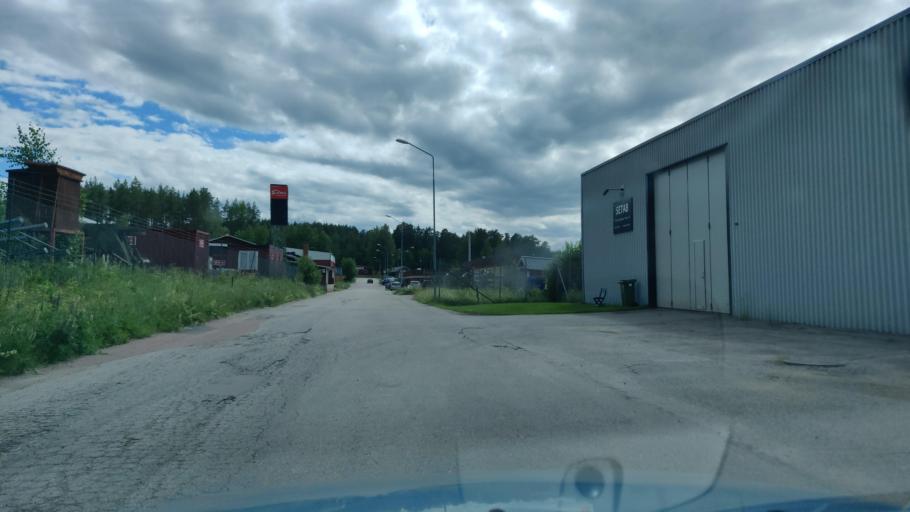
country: SE
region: Vaermland
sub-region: Hagfors Kommun
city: Hagfors
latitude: 60.0443
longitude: 13.7125
